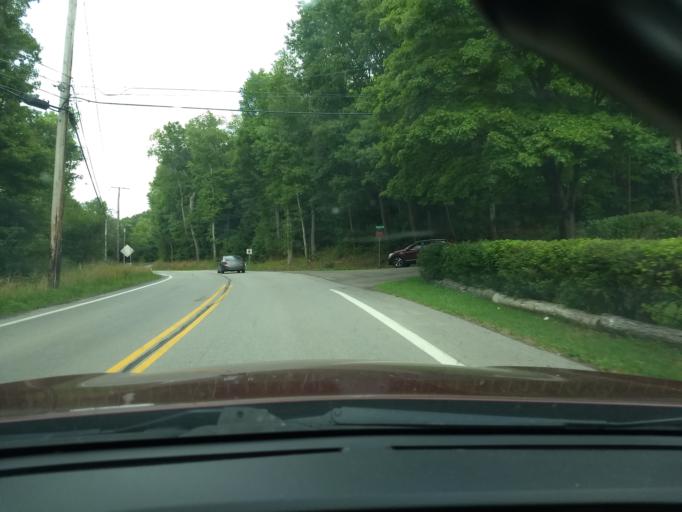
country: US
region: Pennsylvania
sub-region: Allegheny County
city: Bakerstown
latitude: 40.6530
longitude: -79.9069
